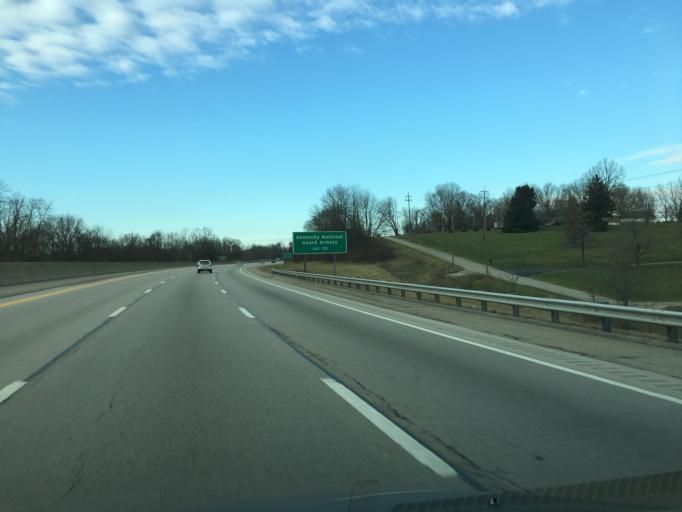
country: US
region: Kentucky
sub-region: Boone County
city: Walton
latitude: 38.8450
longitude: -84.6204
